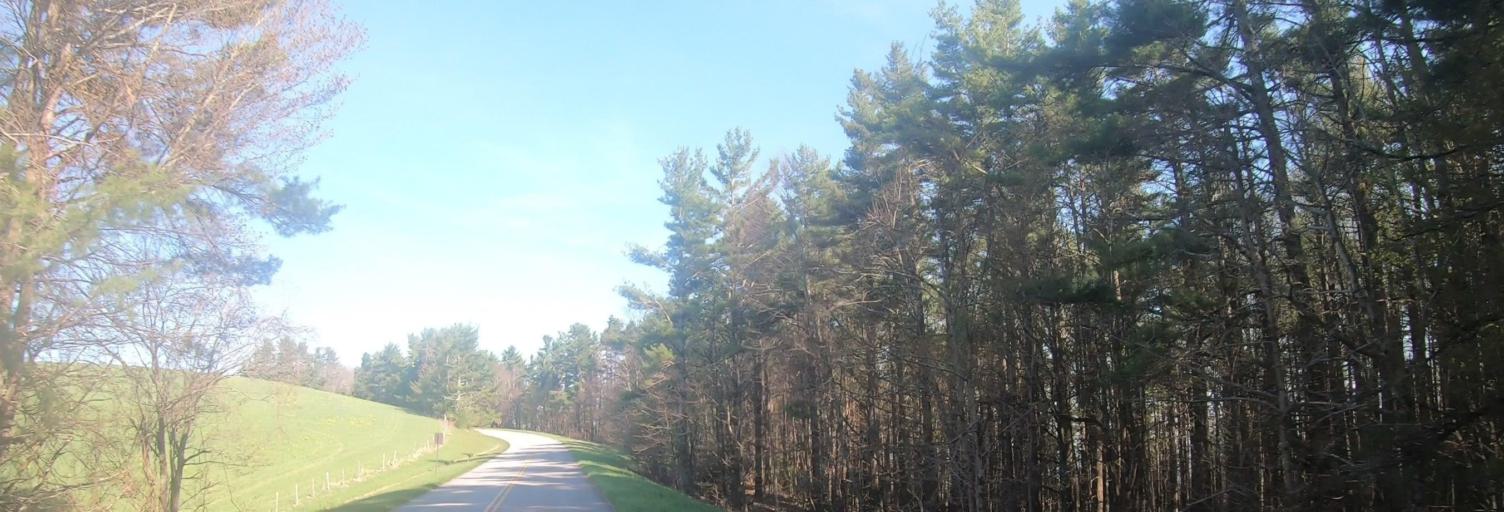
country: US
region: North Carolina
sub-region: Watauga County
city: Boone
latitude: 36.2254
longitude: -81.5190
